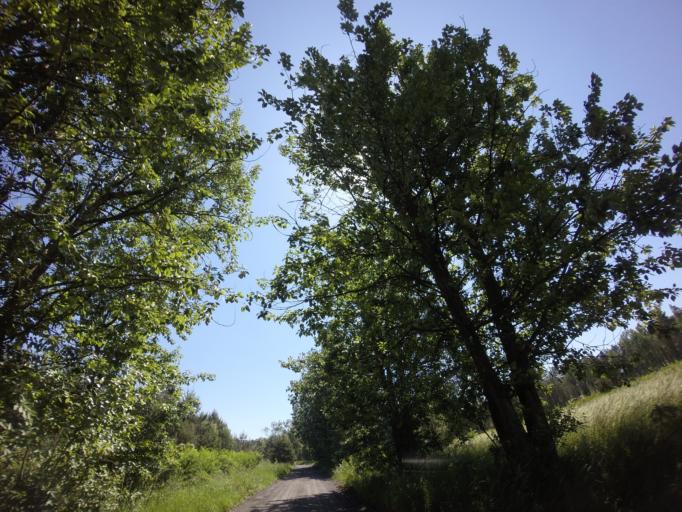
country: PL
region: West Pomeranian Voivodeship
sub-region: Powiat walecki
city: Miroslawiec
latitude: 53.2478
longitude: 16.0247
